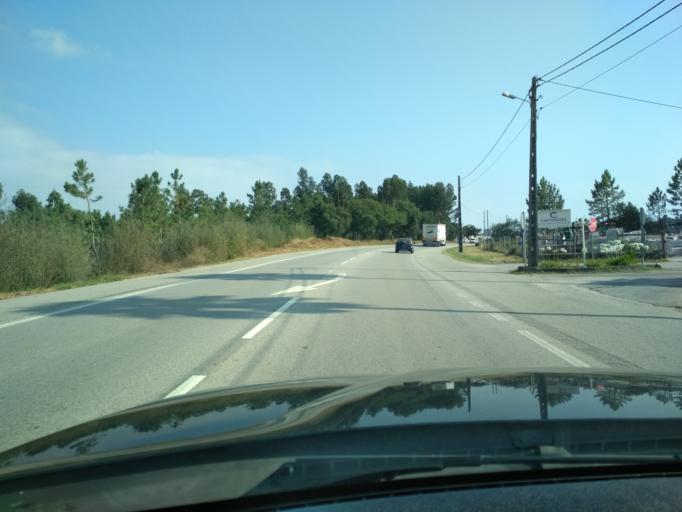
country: PT
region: Aveiro
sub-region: Mealhada
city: Pampilhosa do Botao
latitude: 40.3325
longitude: -8.4507
